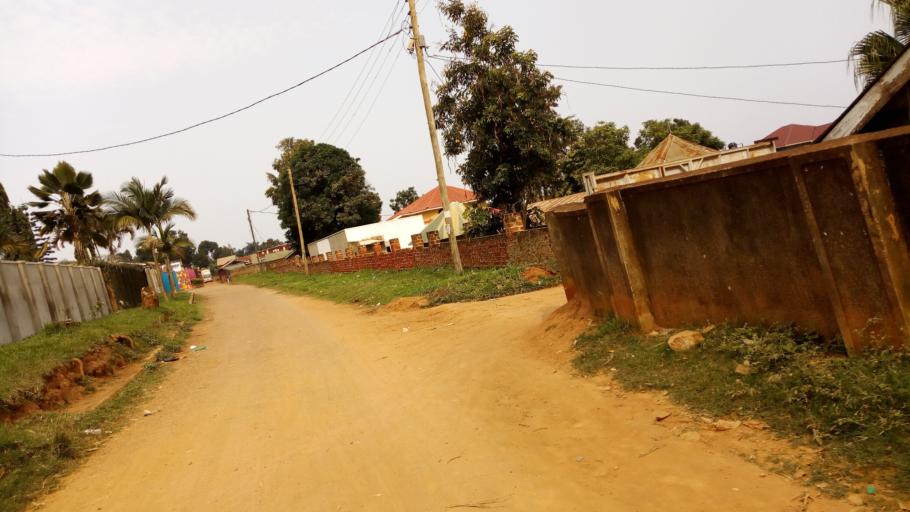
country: UG
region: Central Region
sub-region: Wakiso District
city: Kireka
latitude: 0.3112
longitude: 32.6425
